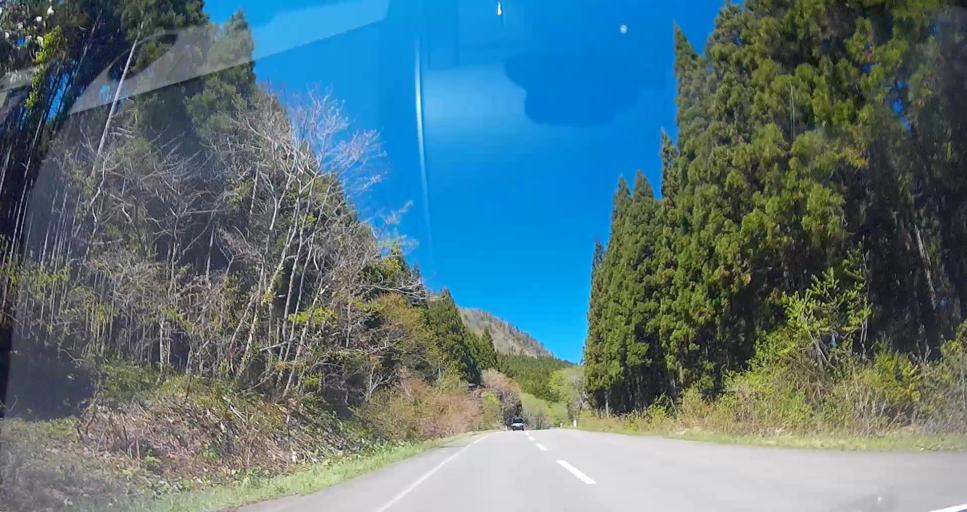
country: JP
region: Aomori
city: Mutsu
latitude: 41.3312
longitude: 141.4125
